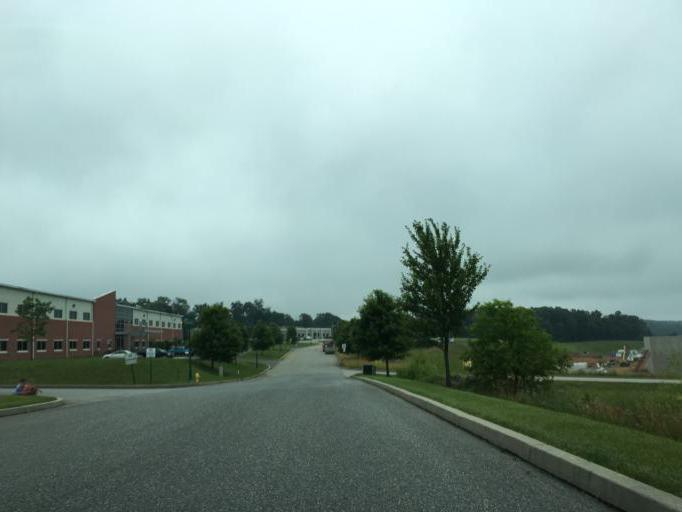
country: US
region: Pennsylvania
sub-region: York County
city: Shrewsbury
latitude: 39.7740
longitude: -76.6593
